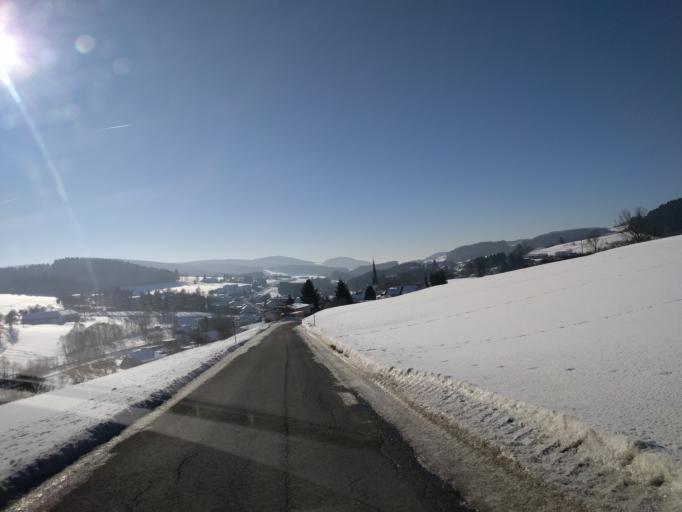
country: AT
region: Upper Austria
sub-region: Politischer Bezirk Urfahr-Umgebung
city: Zwettl an der Rodl
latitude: 48.4704
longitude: 14.2743
